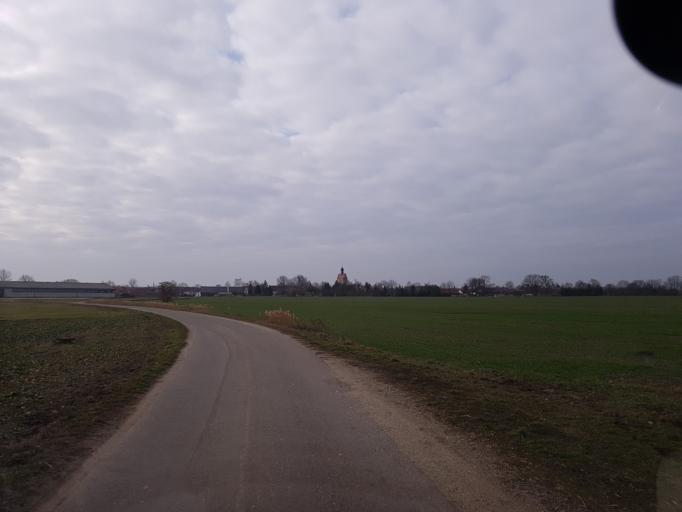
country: DE
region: Brandenburg
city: Doberlug-Kirchhain
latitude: 51.6578
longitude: 13.5410
